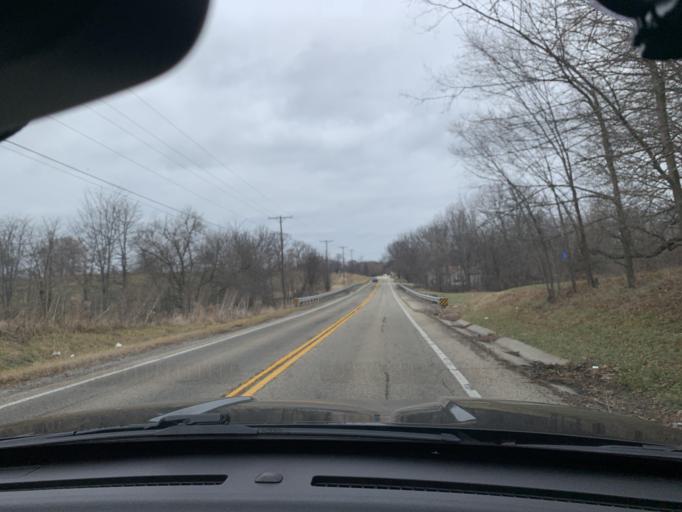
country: US
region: Illinois
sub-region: Sangamon County
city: Jerome
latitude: 39.7255
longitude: -89.6909
